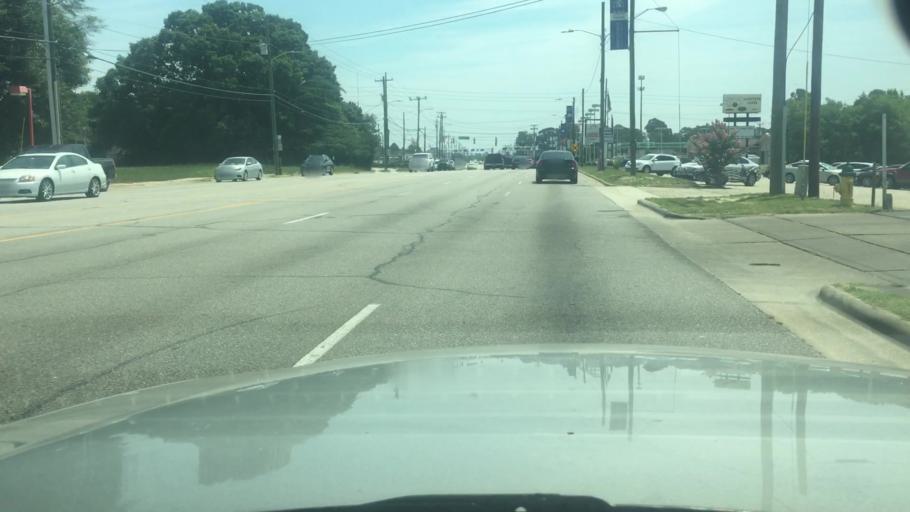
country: US
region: North Carolina
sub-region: Cumberland County
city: Fayetteville
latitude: 35.0442
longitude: -78.9370
